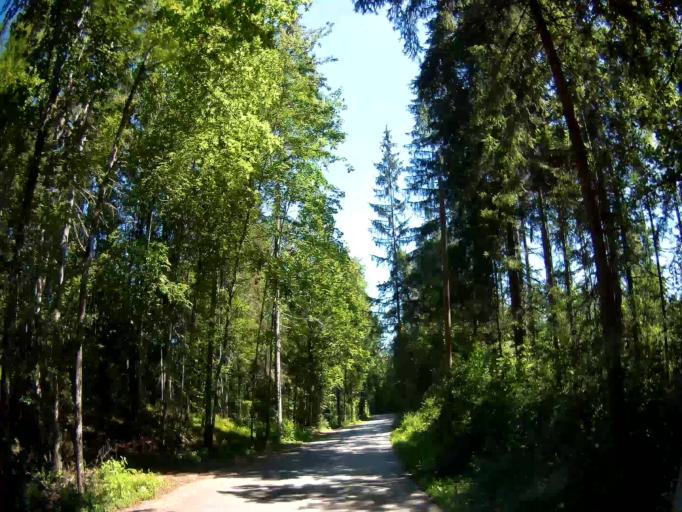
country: AT
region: Carinthia
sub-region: Politischer Bezirk Volkermarkt
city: Gallizien
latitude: 46.5418
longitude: 14.5101
